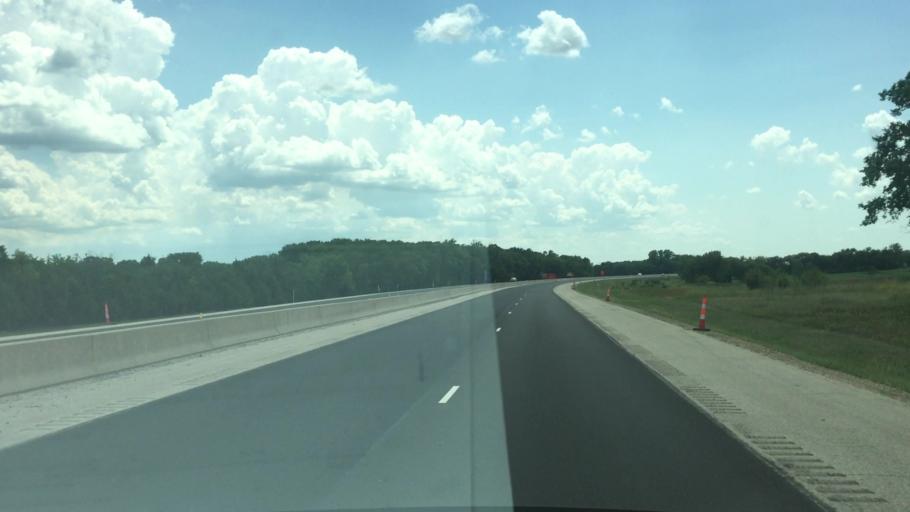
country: US
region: Kansas
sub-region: Lyon County
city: Emporia
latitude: 38.5038
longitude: -96.1515
